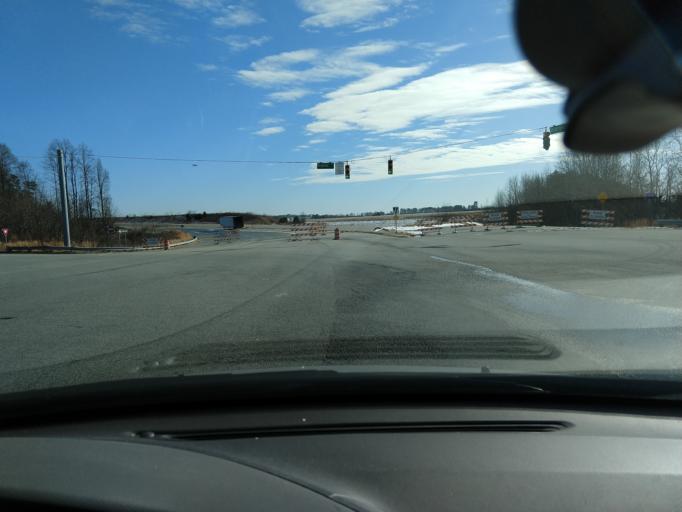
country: US
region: North Carolina
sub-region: Guilford County
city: Oak Ridge
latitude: 36.1069
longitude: -79.9555
